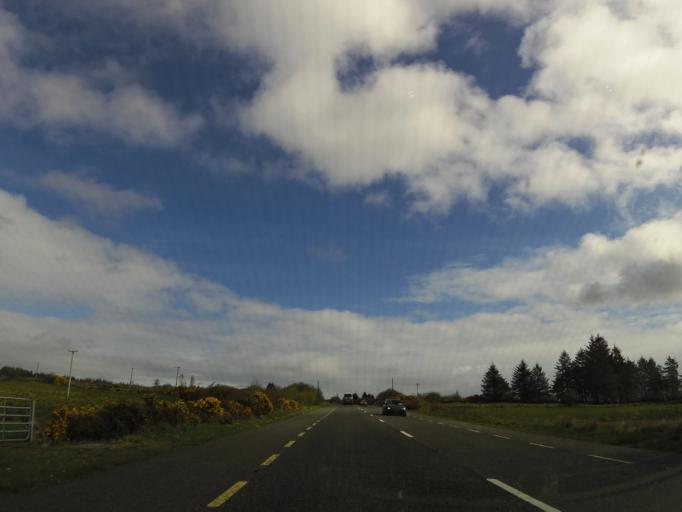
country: IE
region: Connaught
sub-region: Maigh Eo
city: Ballyhaunis
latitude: 53.9029
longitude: -8.7970
